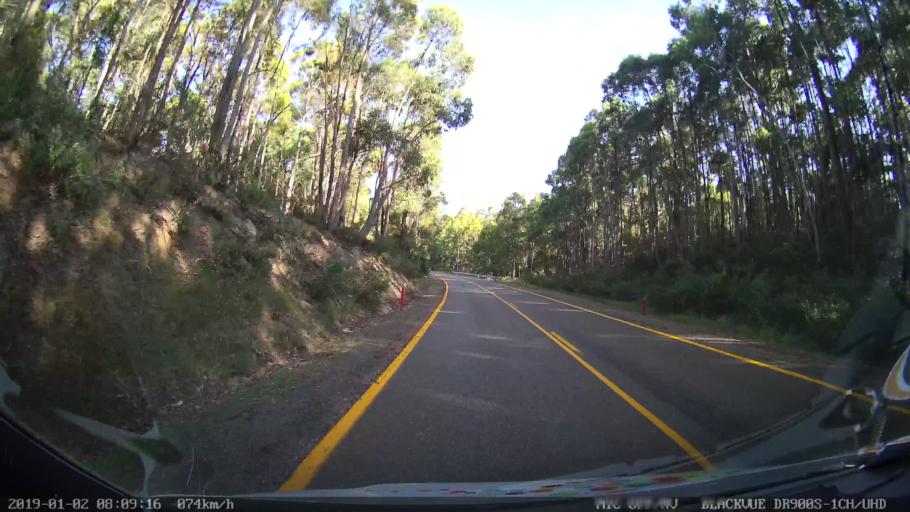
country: AU
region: New South Wales
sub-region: Tumut Shire
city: Tumut
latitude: -35.6085
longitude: 148.3807
